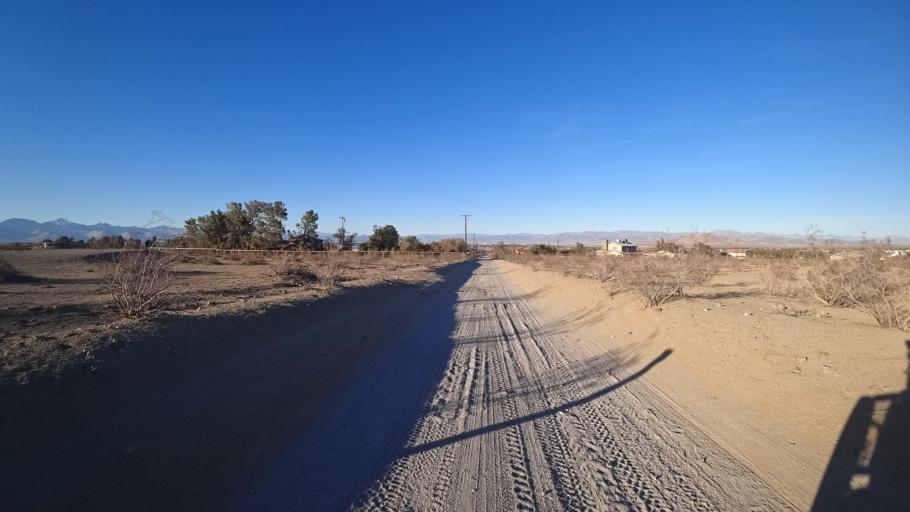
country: US
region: California
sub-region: Kern County
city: Ridgecrest
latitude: 35.5824
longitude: -117.6615
